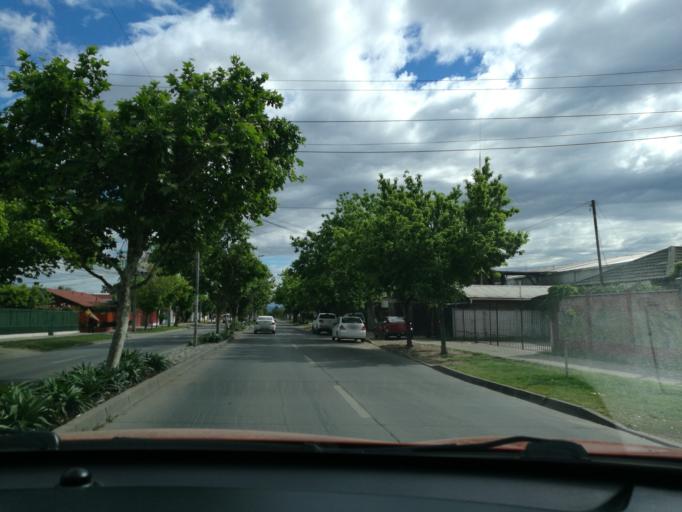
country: CL
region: O'Higgins
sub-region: Provincia de Cachapoal
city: Rancagua
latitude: -34.1656
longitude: -70.7342
